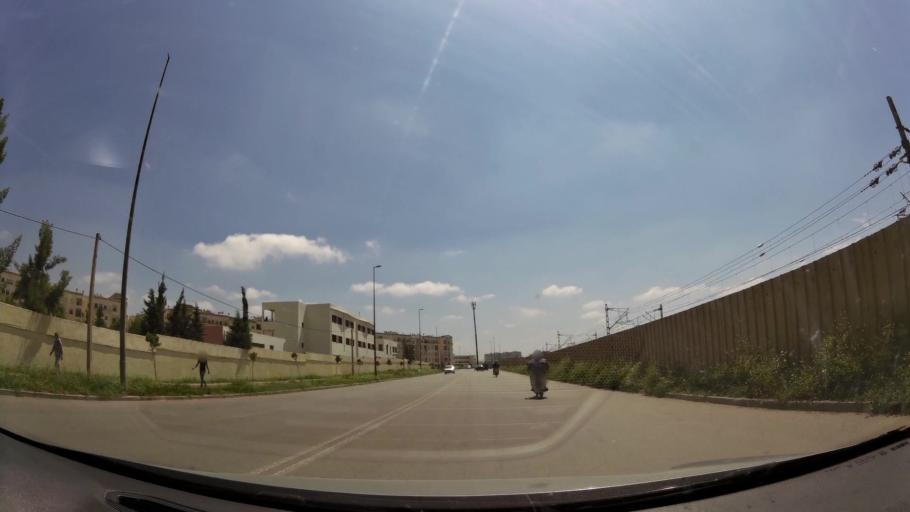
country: MA
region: Fes-Boulemane
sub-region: Fes
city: Fes
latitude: 34.0172
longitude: -5.0429
